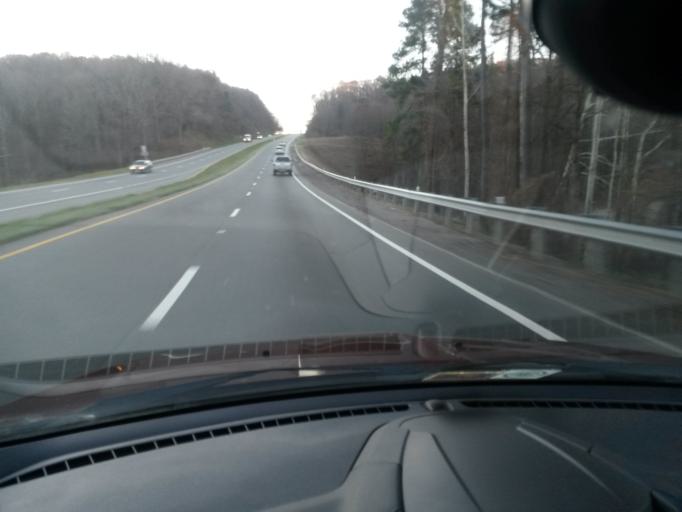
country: US
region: Virginia
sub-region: Roanoke County
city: Narrows
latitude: 37.1033
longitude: -79.9425
